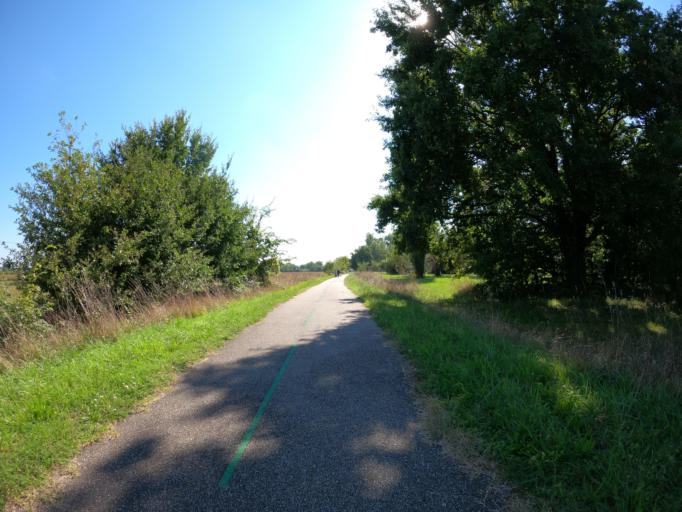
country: FR
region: Aquitaine
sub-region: Departement du Lot-et-Garonne
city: Casseneuil
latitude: 44.4314
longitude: 0.6404
